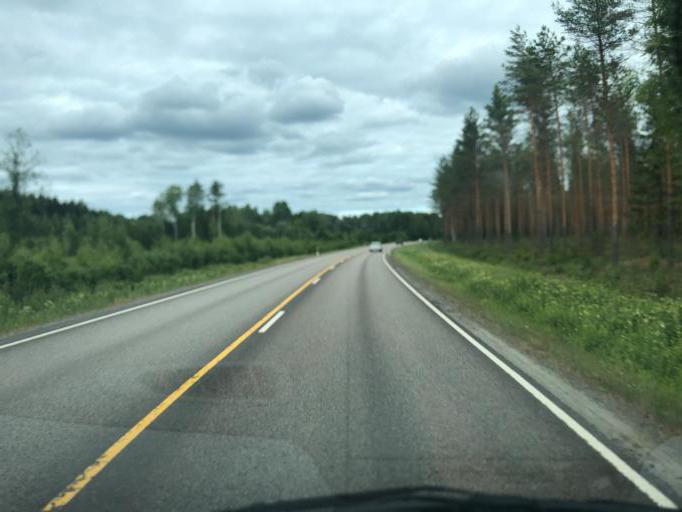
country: FI
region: Kymenlaakso
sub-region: Kouvola
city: Kouvola
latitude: 61.0180
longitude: 26.9563
